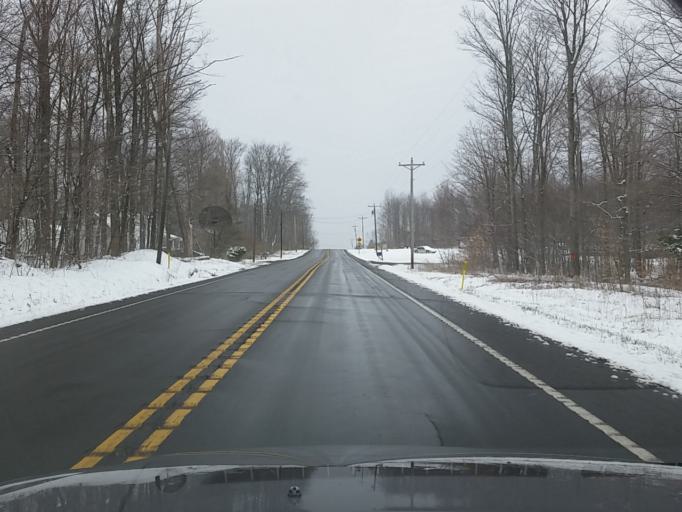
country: US
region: Pennsylvania
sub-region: Sullivan County
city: Laporte
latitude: 41.3905
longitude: -76.5044
